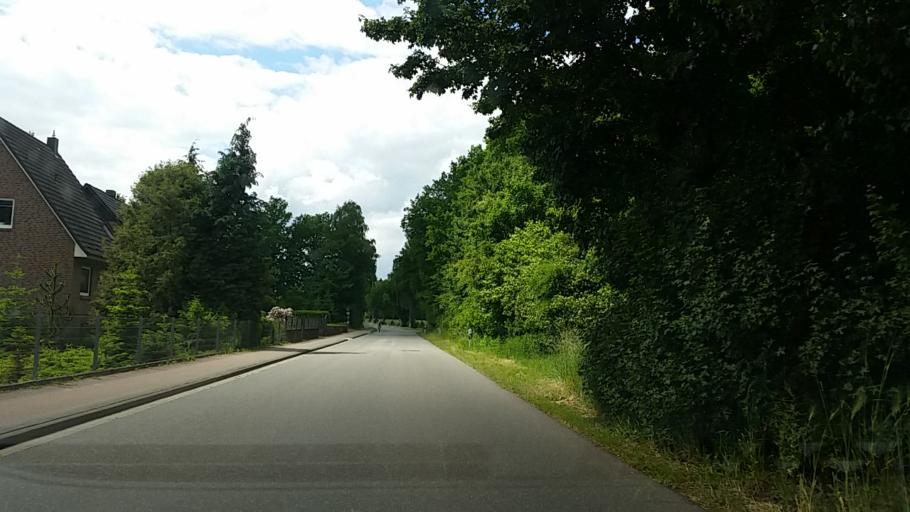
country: DE
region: Schleswig-Holstein
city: Dahmker
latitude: 53.5988
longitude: 10.4330
